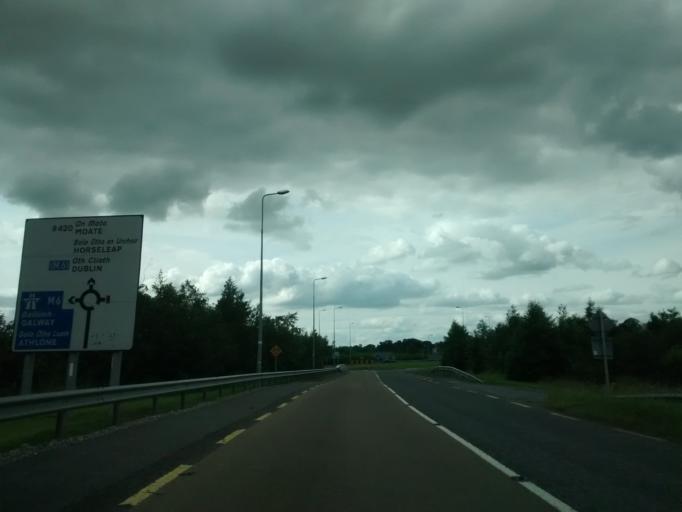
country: IE
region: Leinster
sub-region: An Iarmhi
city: Moate
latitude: 53.3850
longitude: -7.6816
